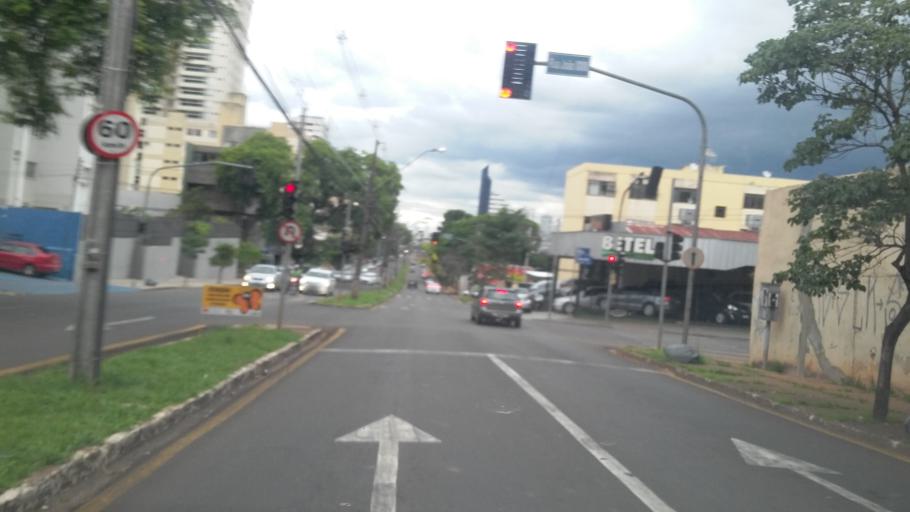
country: BR
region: Parana
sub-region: Londrina
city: Londrina
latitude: -23.3090
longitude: -51.1706
